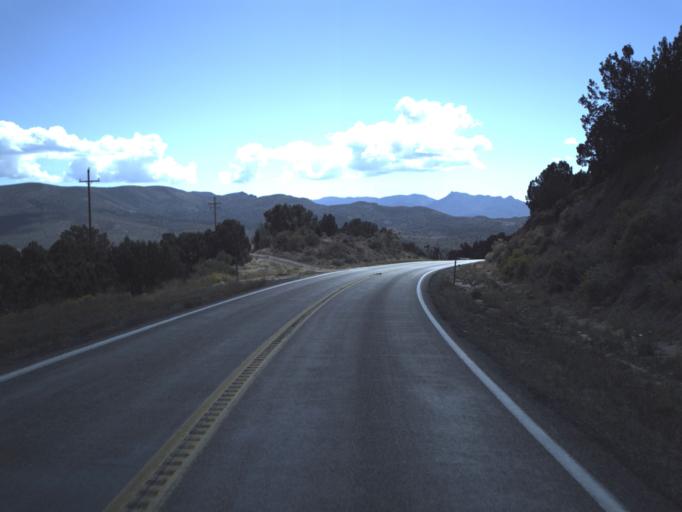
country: US
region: Utah
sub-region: Washington County
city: Enterprise
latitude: 37.5226
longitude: -113.6397
